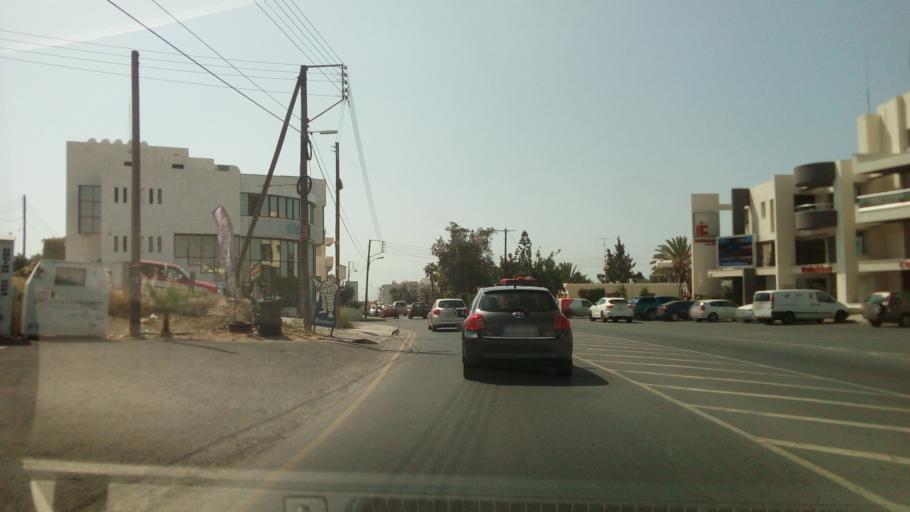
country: CY
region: Limassol
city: Limassol
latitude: 34.7083
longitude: 33.0245
